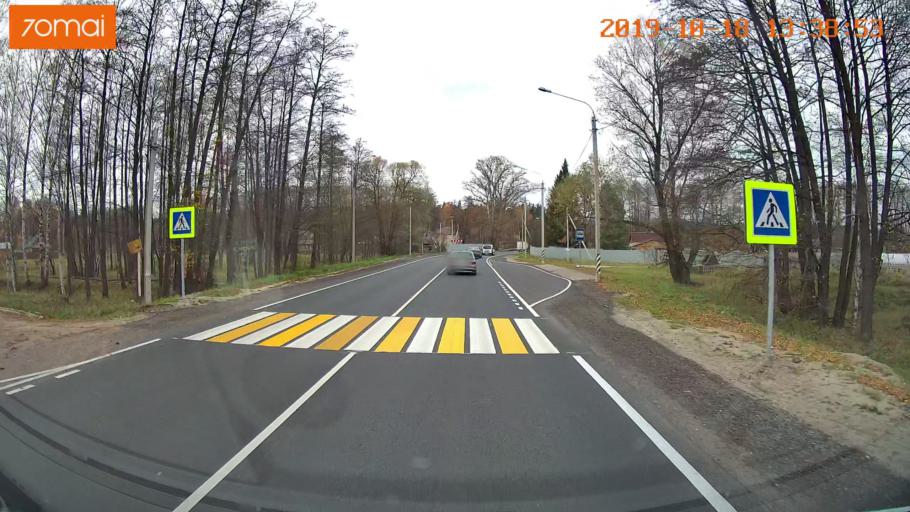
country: RU
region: Rjazan
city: Solotcha
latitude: 54.8938
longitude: 40.0016
